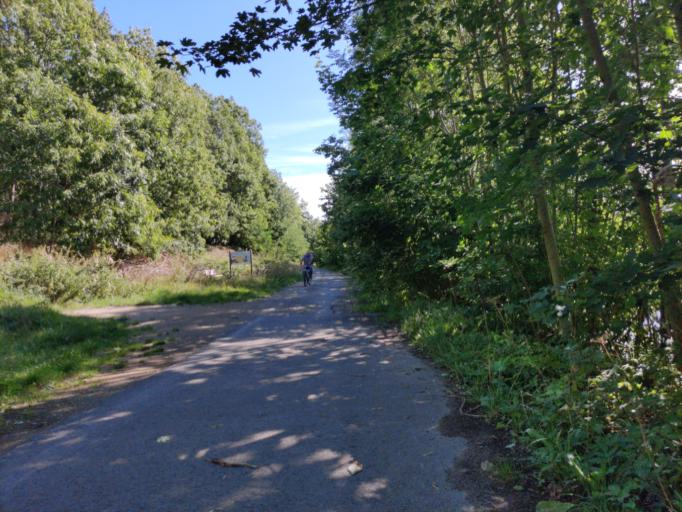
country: DE
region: Lower Saxony
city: Holle
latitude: 52.1043
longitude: 10.1670
